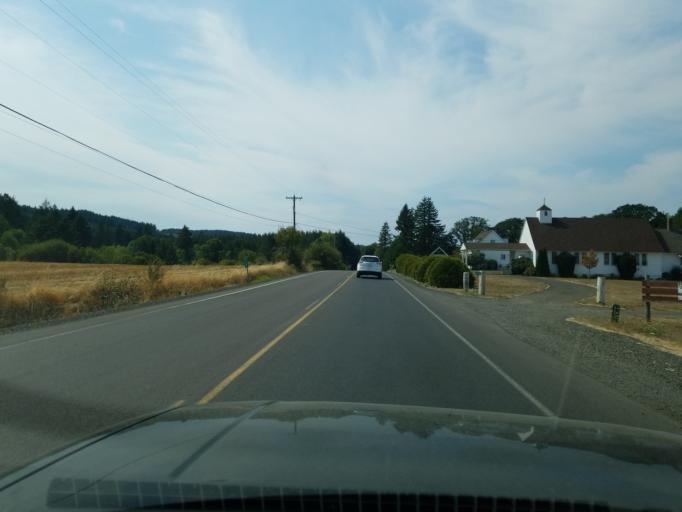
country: US
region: Oregon
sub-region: Polk County
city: Grand Ronde
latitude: 45.0800
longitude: -123.6121
